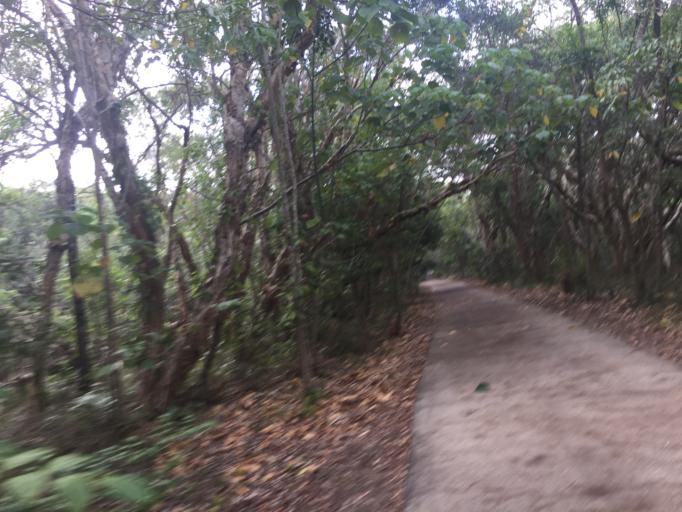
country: AU
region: Queensland
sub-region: Sunshine Coast
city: Coolum Beach
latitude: -26.5726
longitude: 153.0972
